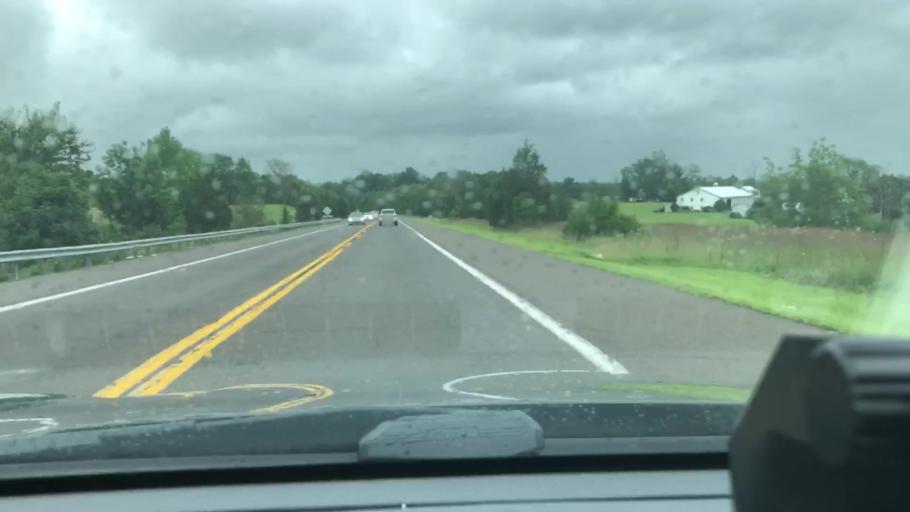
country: US
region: Pennsylvania
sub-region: Bucks County
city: Spinnerstown
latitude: 40.4210
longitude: -75.4487
